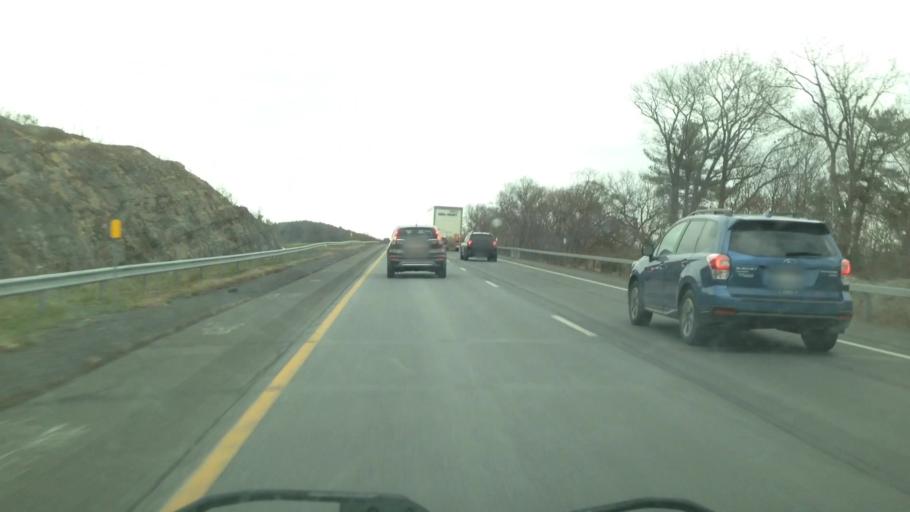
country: US
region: New York
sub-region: Greene County
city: Jefferson Heights
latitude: 42.2749
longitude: -73.8732
